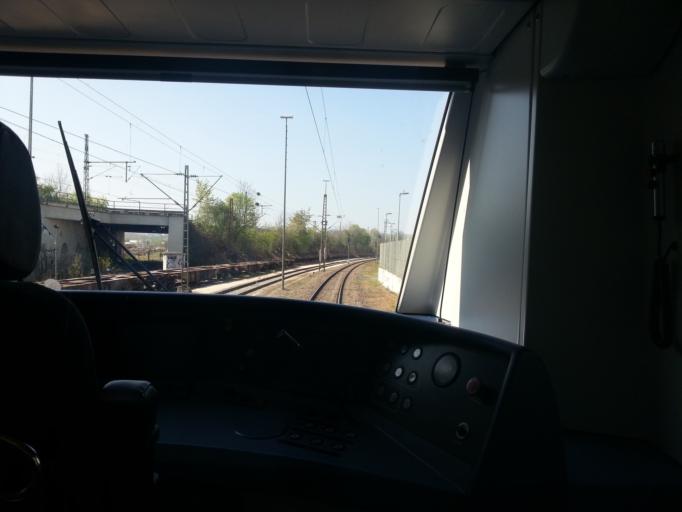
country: DE
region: Baden-Wuerttemberg
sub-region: Regierungsbezirk Stuttgart
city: Stuttgart-Ost
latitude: 48.7953
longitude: 9.2340
